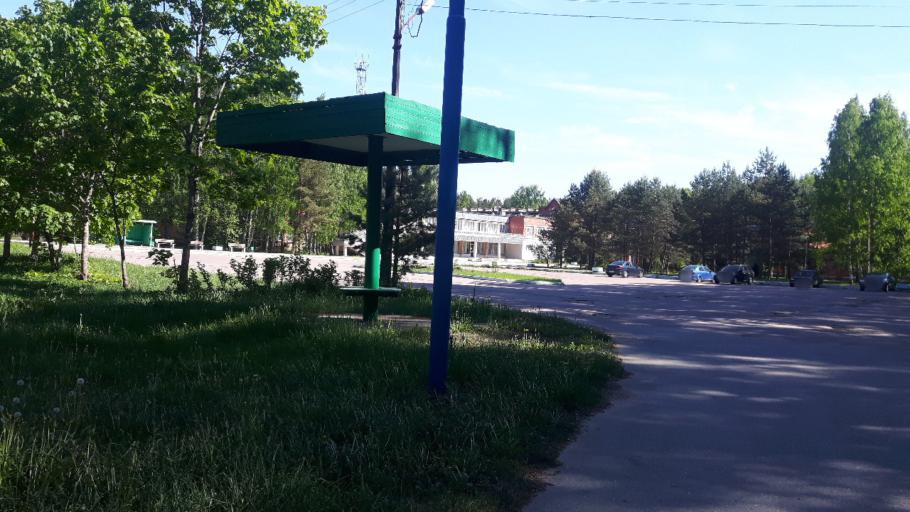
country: RU
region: Leningrad
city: Sista-Palkino
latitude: 59.7643
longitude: 28.7399
